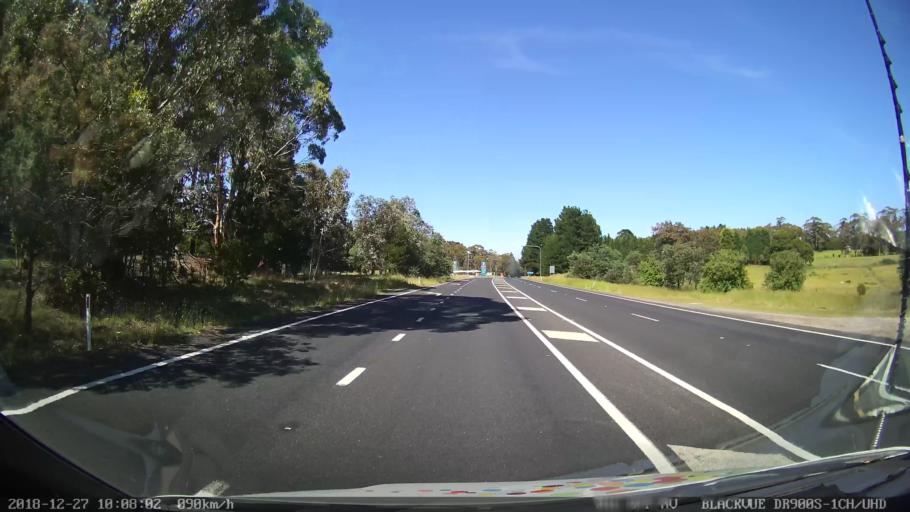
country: AU
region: New South Wales
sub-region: Lithgow
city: Portland
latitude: -33.4450
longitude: 149.8317
